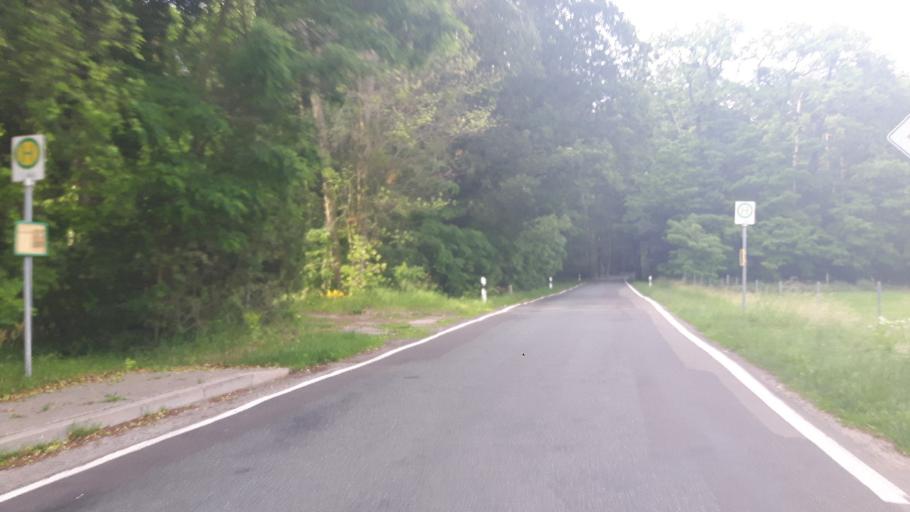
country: DE
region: Brandenburg
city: Hohenfinow
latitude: 52.7793
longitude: 13.8937
